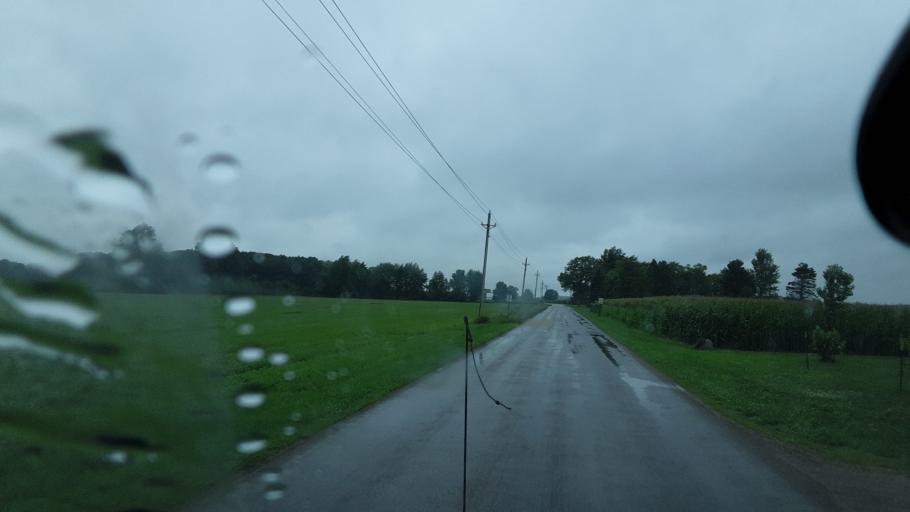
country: US
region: Indiana
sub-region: Adams County
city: Berne
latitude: 40.7182
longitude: -84.8533
